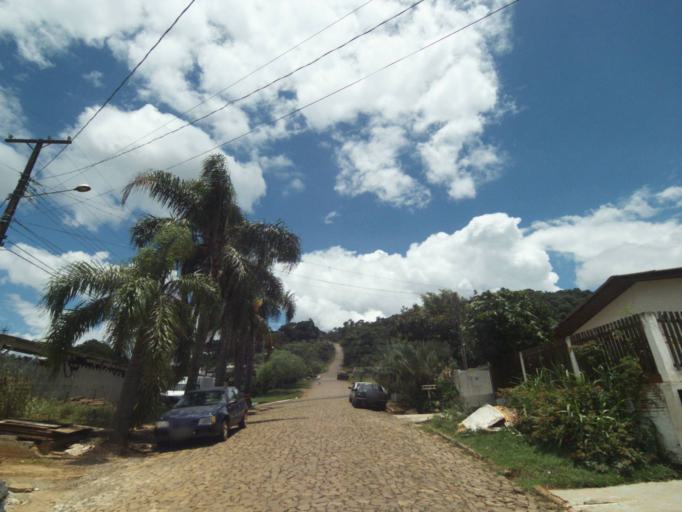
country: BR
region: Parana
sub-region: Pinhao
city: Pinhao
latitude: -26.1582
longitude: -51.5578
